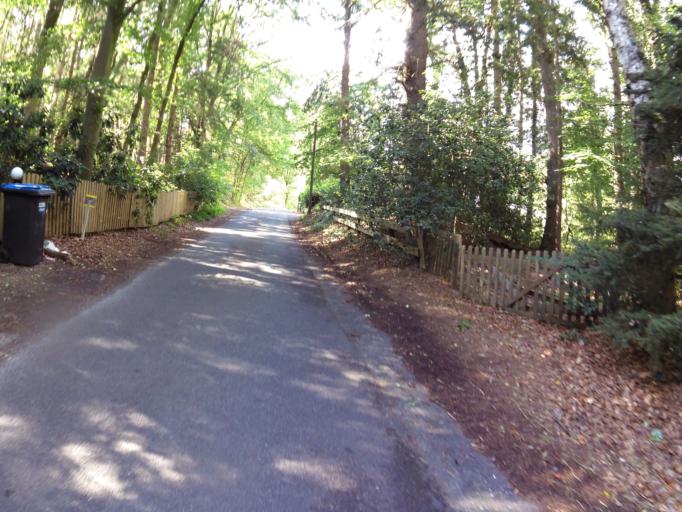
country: DE
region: Lower Saxony
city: Seedorf
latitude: 53.3325
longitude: 9.1982
